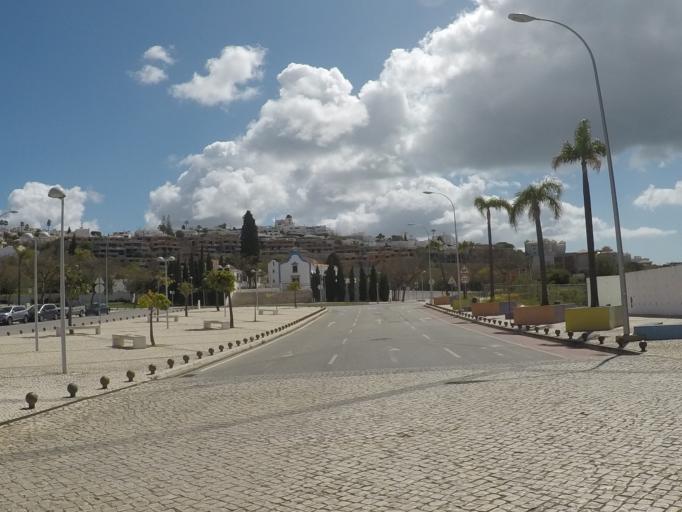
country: PT
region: Faro
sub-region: Albufeira
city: Albufeira
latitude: 37.0854
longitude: -8.2660
